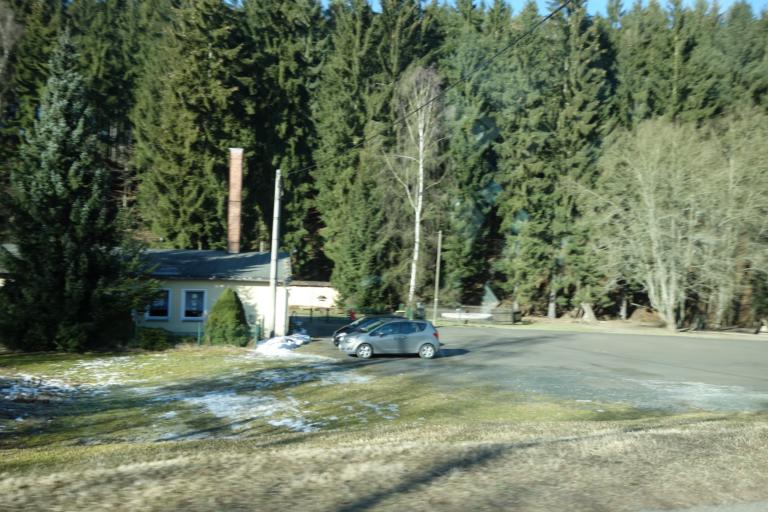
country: DE
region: Saxony
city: Frankenstein
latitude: 50.9359
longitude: 13.2064
